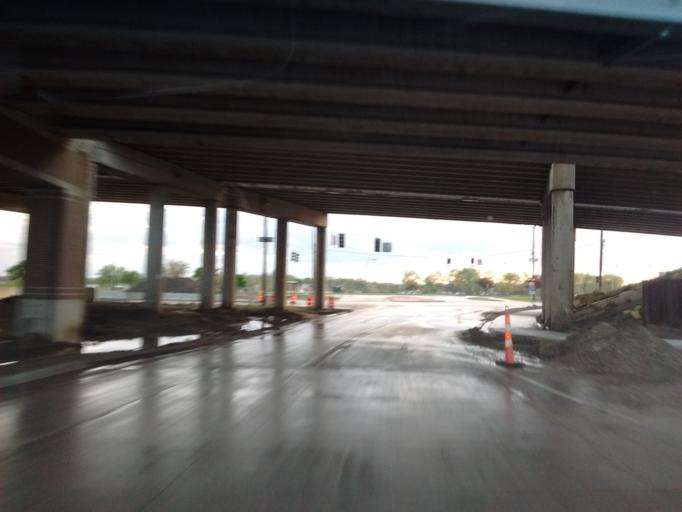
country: US
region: Iowa
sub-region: Woodbury County
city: Sioux City
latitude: 42.4871
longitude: -96.3948
